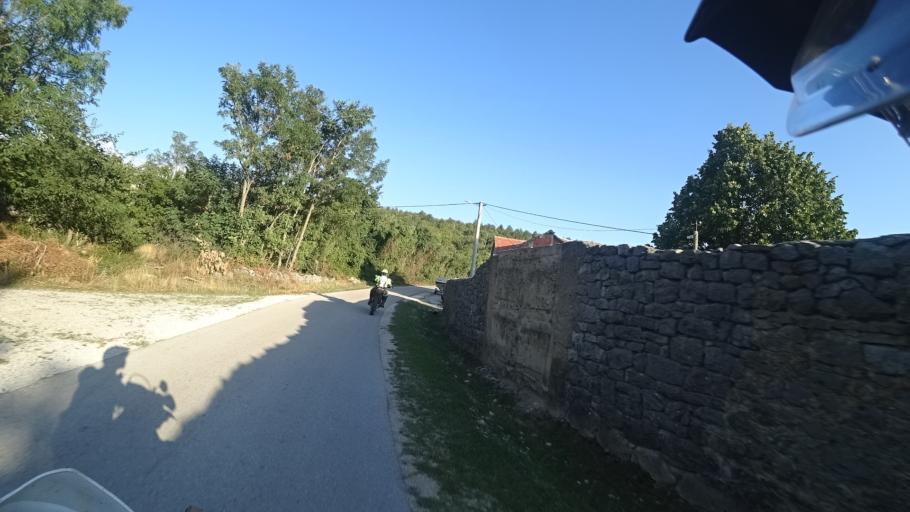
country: HR
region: Sibensko-Kniniska
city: Knin
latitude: 44.0656
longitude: 16.1757
